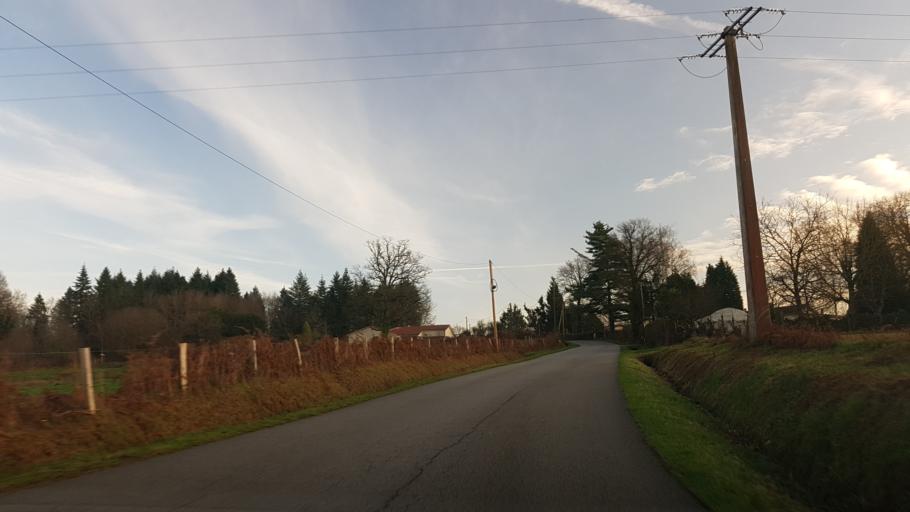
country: FR
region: Limousin
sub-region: Departement de la Haute-Vienne
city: Saint-Junien
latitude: 45.8987
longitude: 0.8623
